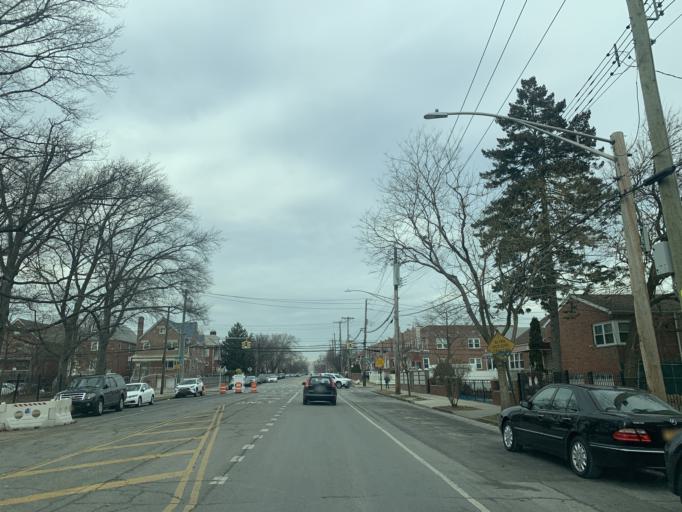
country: US
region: New York
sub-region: Bronx
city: The Bronx
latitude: 40.8591
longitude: -73.8560
